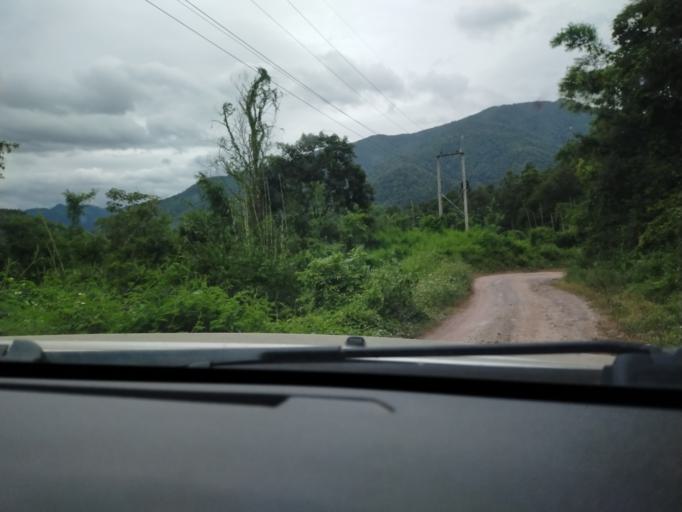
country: TH
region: Nan
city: Chaloem Phra Kiat
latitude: 19.8085
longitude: 101.3622
